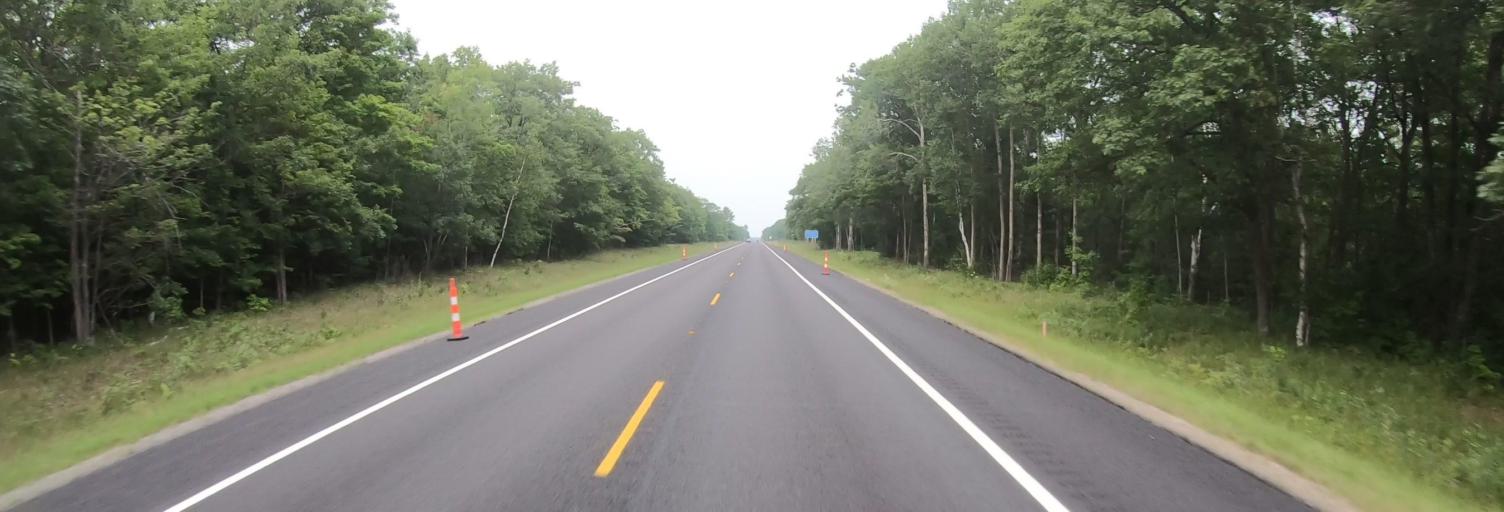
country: US
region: Michigan
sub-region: Mackinac County
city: Saint Ignace
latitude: 45.7053
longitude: -84.7675
